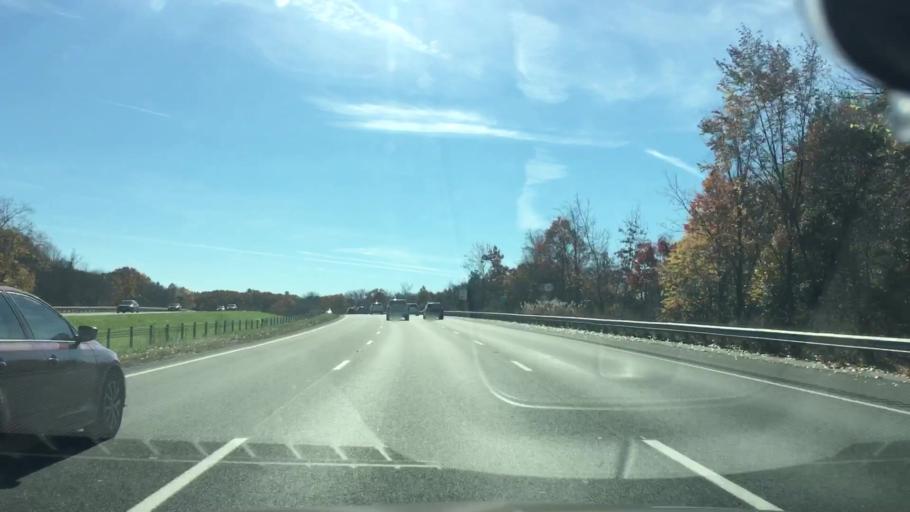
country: US
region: Massachusetts
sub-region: Hampden County
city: Chicopee
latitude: 42.1580
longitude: -72.6476
